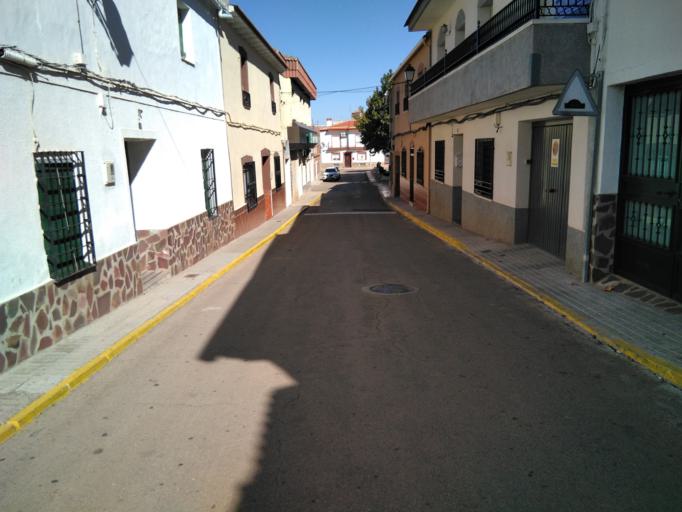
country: ES
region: Castille-La Mancha
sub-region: Provincia de Ciudad Real
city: Ballesteros de Calatrava
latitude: 38.8346
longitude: -3.9454
